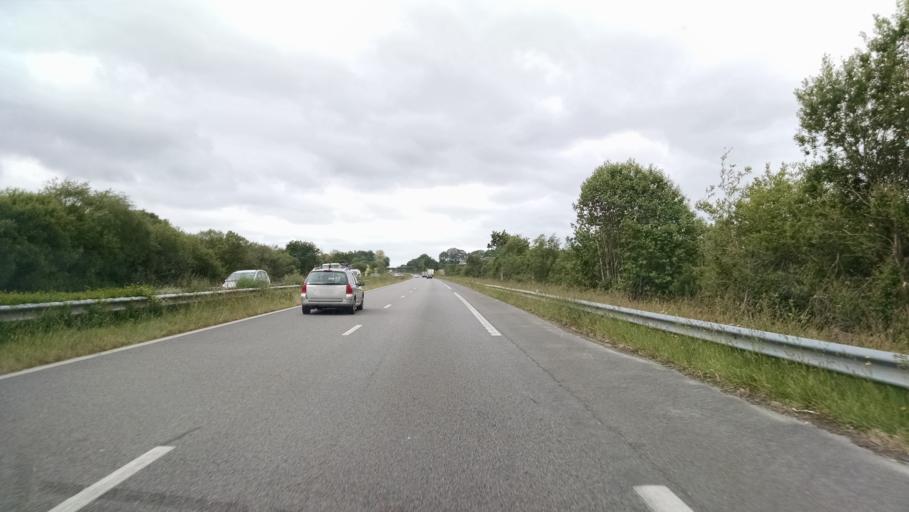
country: FR
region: Brittany
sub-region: Departement du Finistere
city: Le Trevoux
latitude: 47.8761
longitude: -3.6212
